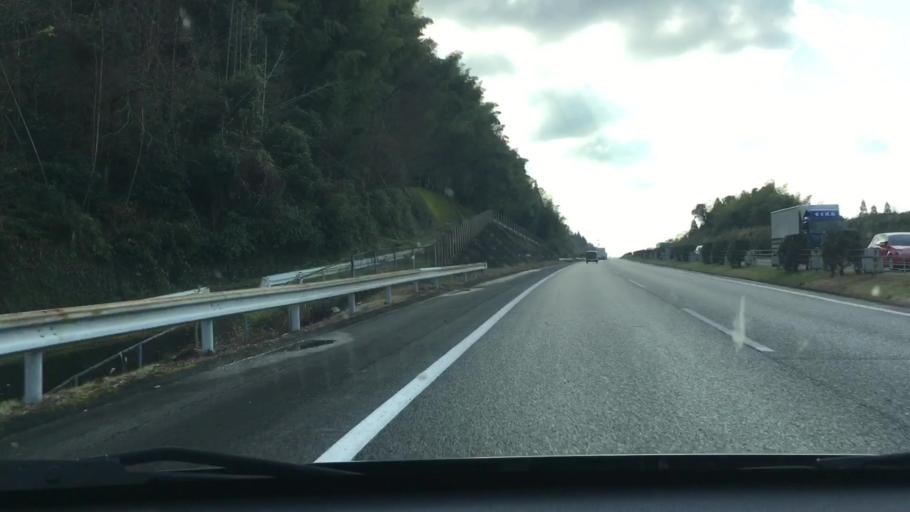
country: JP
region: Kumamoto
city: Yatsushiro
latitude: 32.5314
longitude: 130.6693
